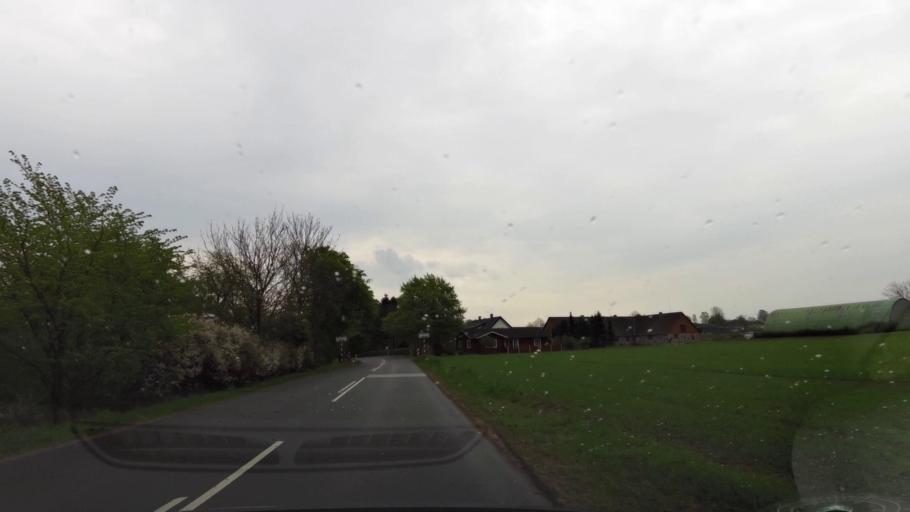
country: DK
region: South Denmark
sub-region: Svendborg Kommune
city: Thuro By
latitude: 55.1566
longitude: 10.6580
